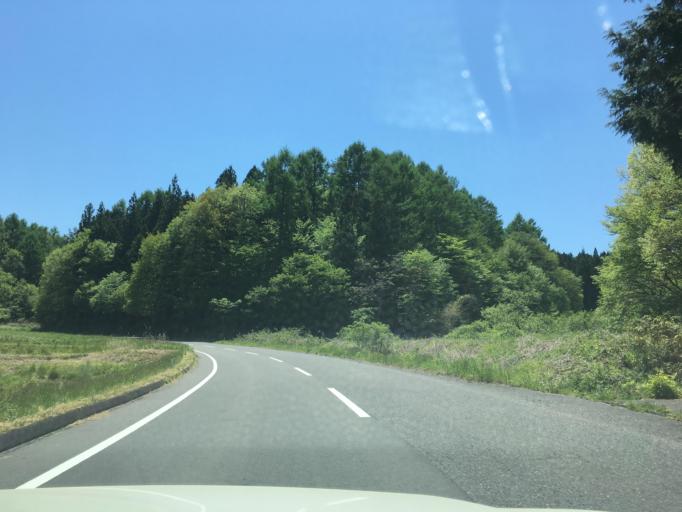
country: JP
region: Fukushima
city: Funehikimachi-funehiki
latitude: 37.3907
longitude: 140.6085
